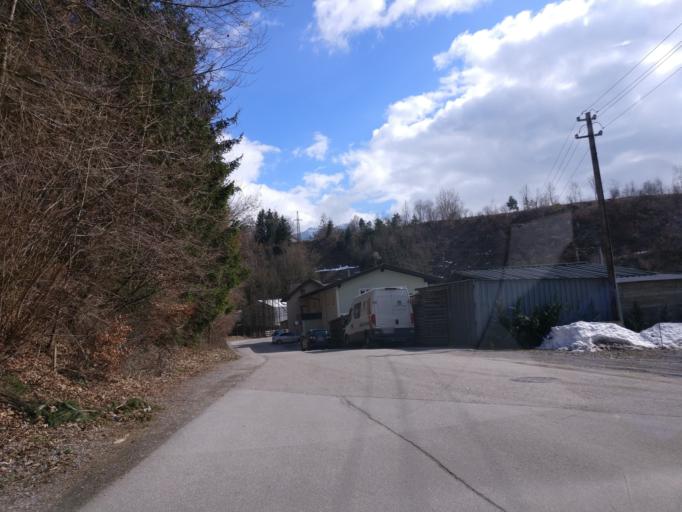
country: AT
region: Salzburg
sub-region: Politischer Bezirk Sankt Johann im Pongau
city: Bischofshofen
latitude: 47.4375
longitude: 13.2159
